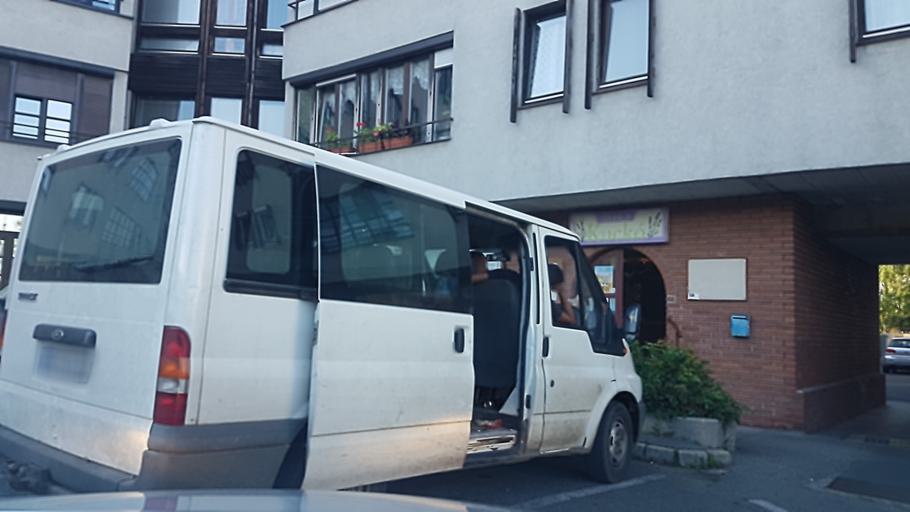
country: HU
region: Gyor-Moson-Sopron
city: Sopron
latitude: 47.6785
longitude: 16.5872
